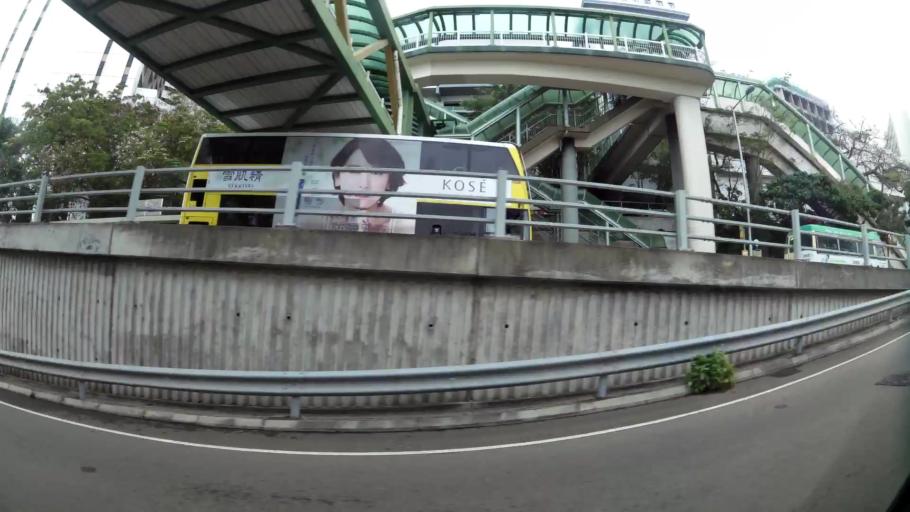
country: HK
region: Central and Western
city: Central
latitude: 22.2697
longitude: 114.1304
